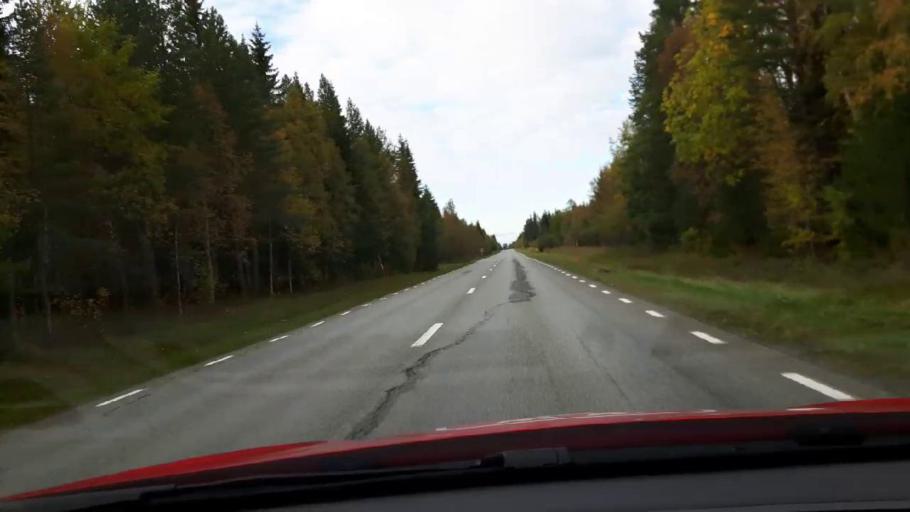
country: SE
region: Jaemtland
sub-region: Krokoms Kommun
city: Valla
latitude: 63.2265
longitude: 14.0164
